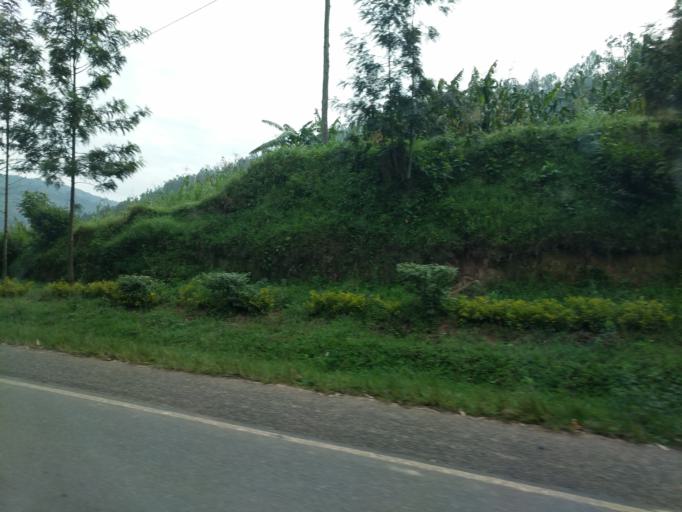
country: RW
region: Northern Province
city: Byumba
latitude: -1.7259
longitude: 29.9199
